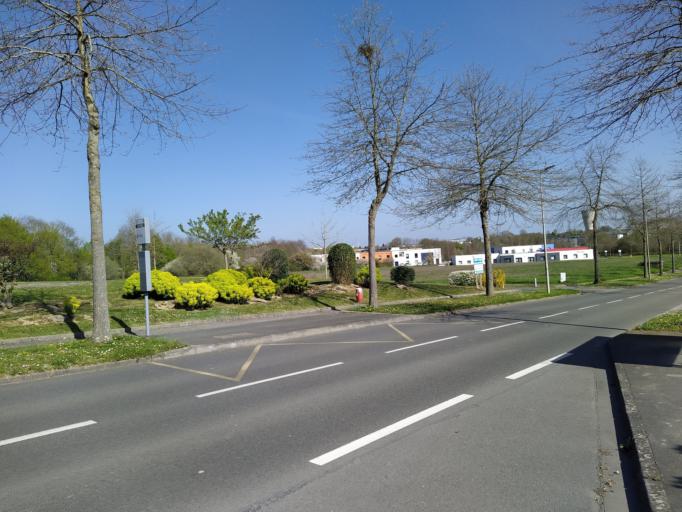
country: FR
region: Pays de la Loire
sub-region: Departement de la Mayenne
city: Laval
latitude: 48.0905
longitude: -0.7622
